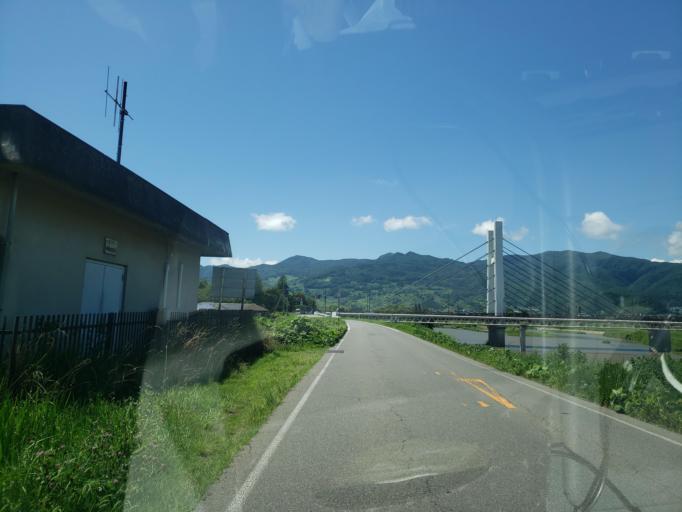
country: JP
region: Nagano
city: Nagano-shi
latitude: 36.5335
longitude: 138.1127
